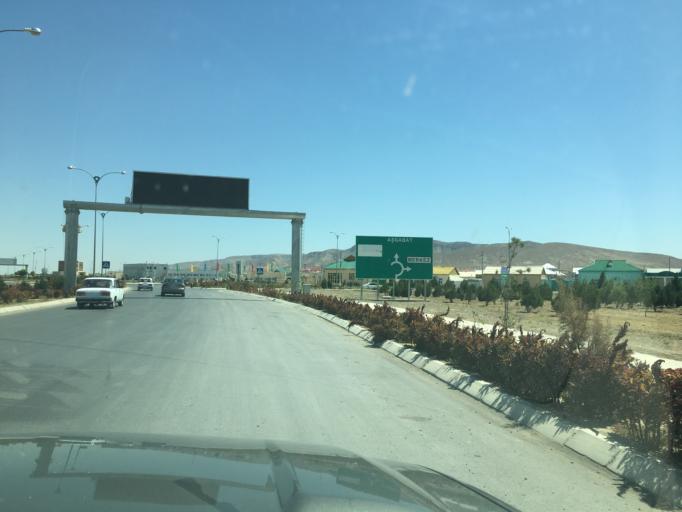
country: TM
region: Balkan
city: Serdar
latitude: 38.9818
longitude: 56.2956
